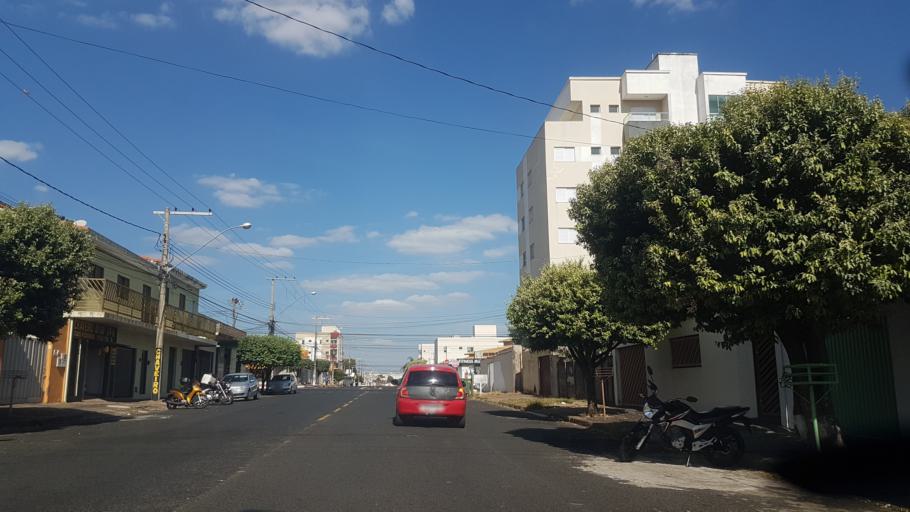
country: BR
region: Minas Gerais
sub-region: Uberlandia
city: Uberlandia
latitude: -18.9036
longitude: -48.2559
